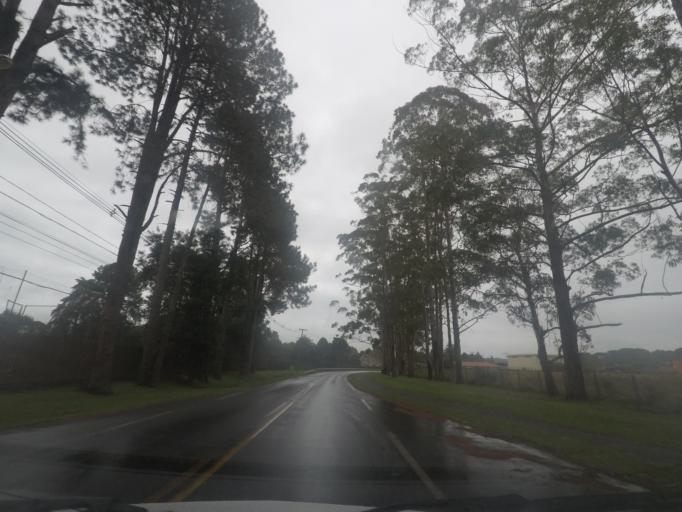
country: BR
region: Parana
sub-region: Quatro Barras
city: Quatro Barras
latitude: -25.3741
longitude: -49.0924
